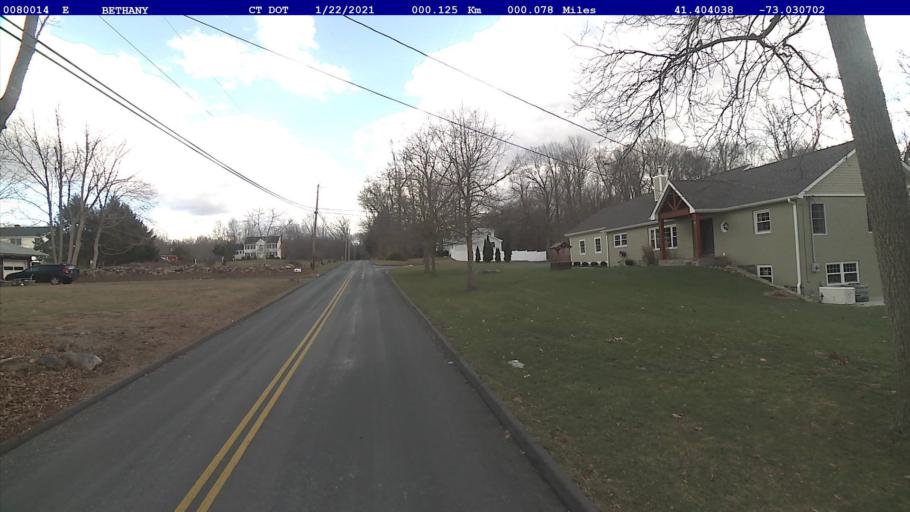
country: US
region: Connecticut
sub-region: New Haven County
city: Seymour
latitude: 41.4040
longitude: -73.0307
